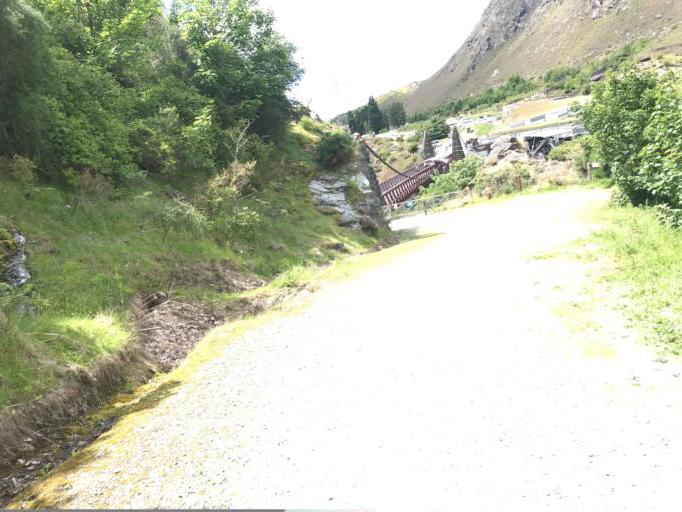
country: NZ
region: Otago
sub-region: Queenstown-Lakes District
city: Arrowtown
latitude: -45.0084
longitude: 168.8987
